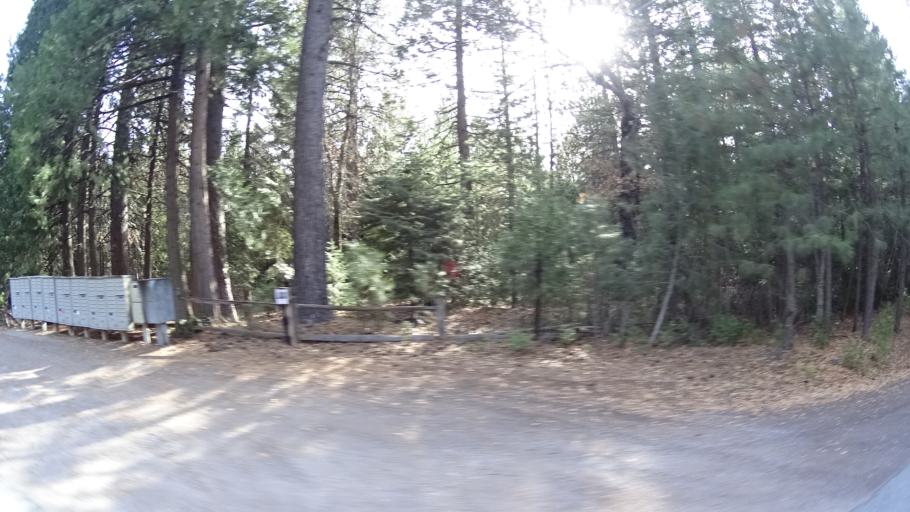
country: US
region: California
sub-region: Siskiyou County
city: Weed
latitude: 41.3833
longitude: -122.3997
